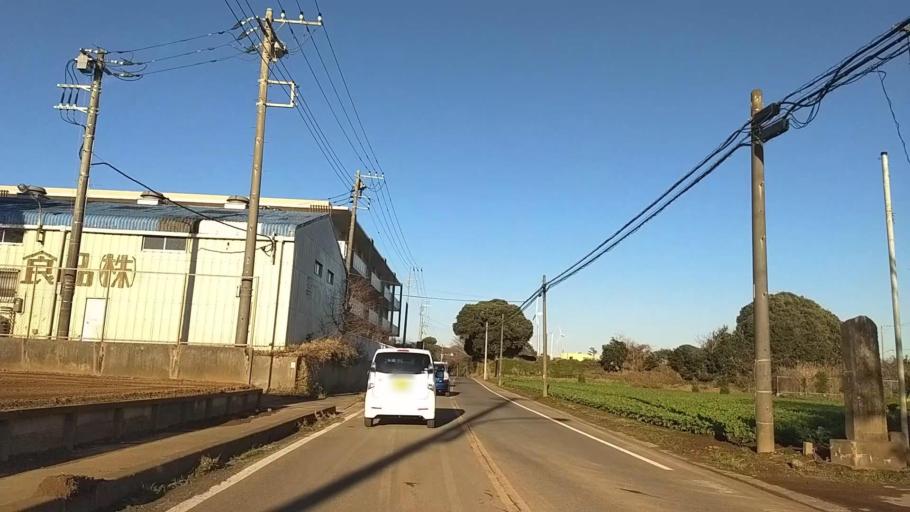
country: JP
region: Chiba
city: Hasaki
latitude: 35.7593
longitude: 140.7478
